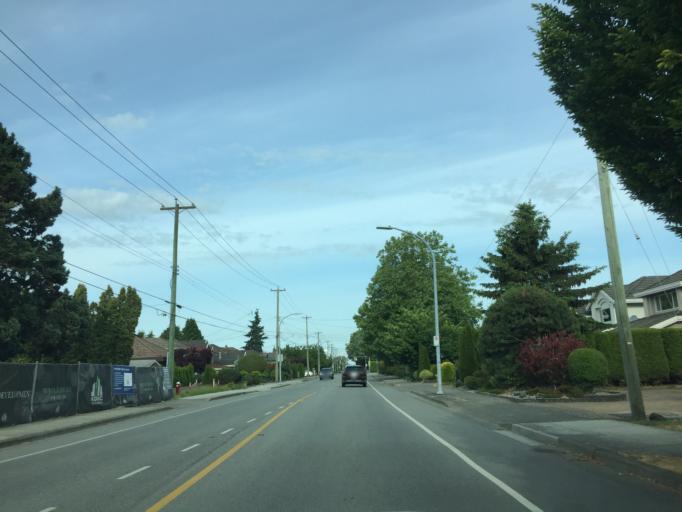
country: CA
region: British Columbia
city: Richmond
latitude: 49.1411
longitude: -123.1600
